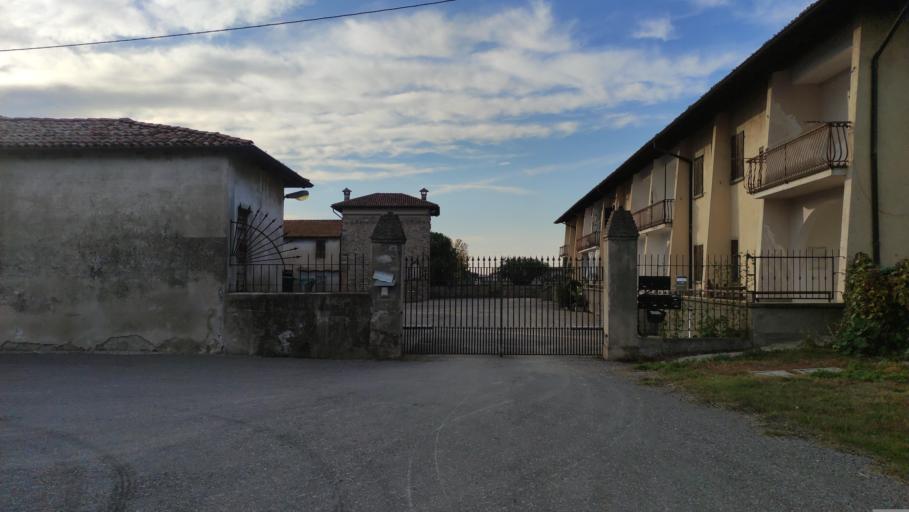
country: IT
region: Lombardy
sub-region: Provincia di Brescia
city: Lodetto
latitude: 45.5640
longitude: 10.0355
